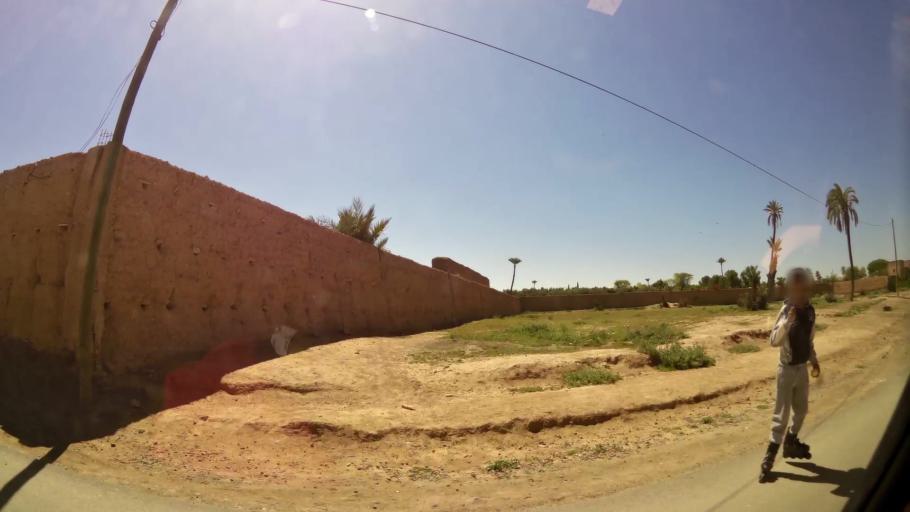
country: MA
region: Marrakech-Tensift-Al Haouz
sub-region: Marrakech
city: Marrakesh
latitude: 31.6694
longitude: -7.9780
